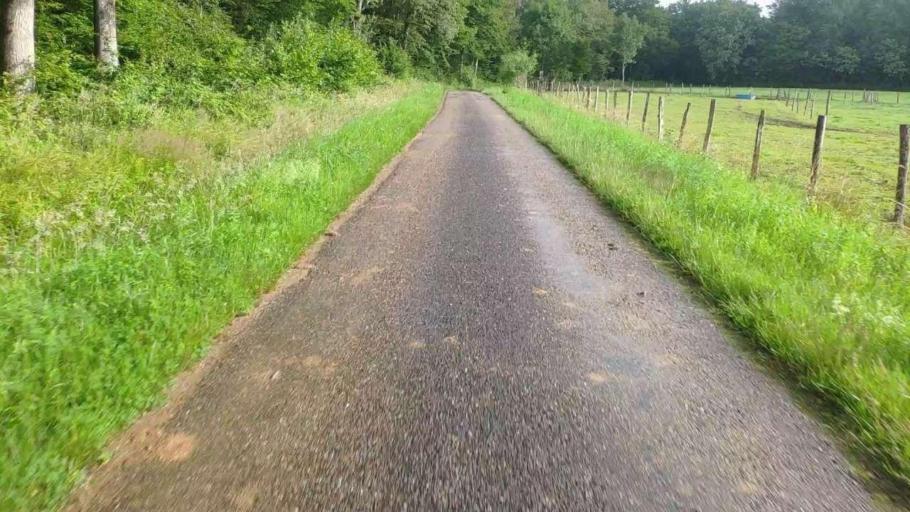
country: FR
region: Franche-Comte
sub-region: Departement du Jura
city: Mont-sous-Vaudrey
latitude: 46.8791
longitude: 5.5219
